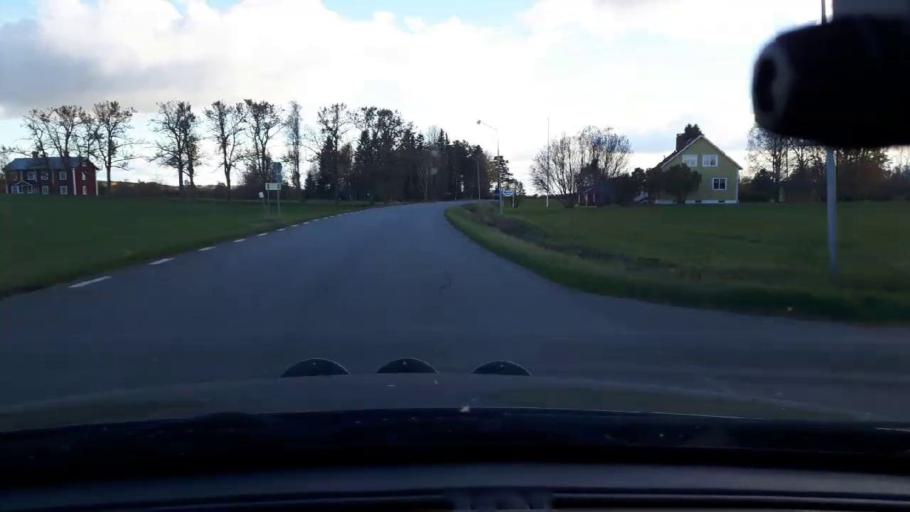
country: SE
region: Jaemtland
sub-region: Bergs Kommun
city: Hoverberg
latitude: 63.0373
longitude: 14.3445
